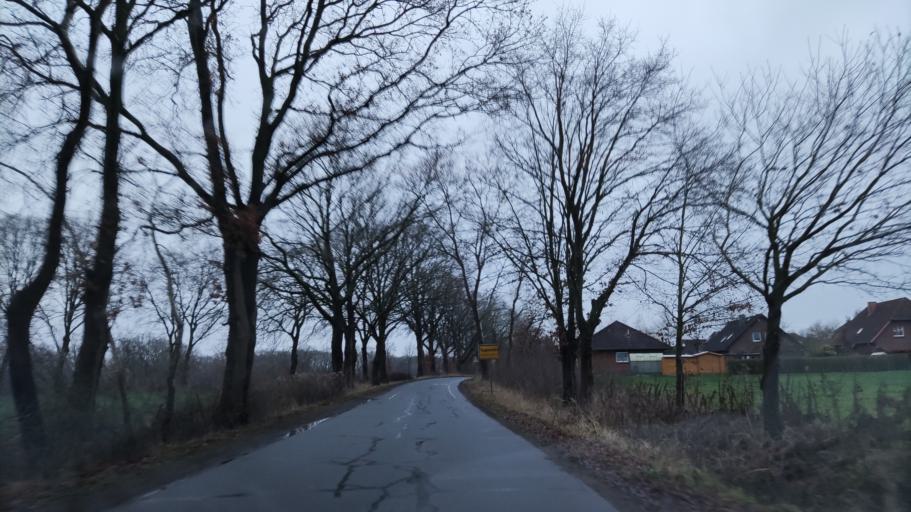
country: DE
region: Lower Saxony
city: Reppenstedt
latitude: 53.2556
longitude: 10.3534
